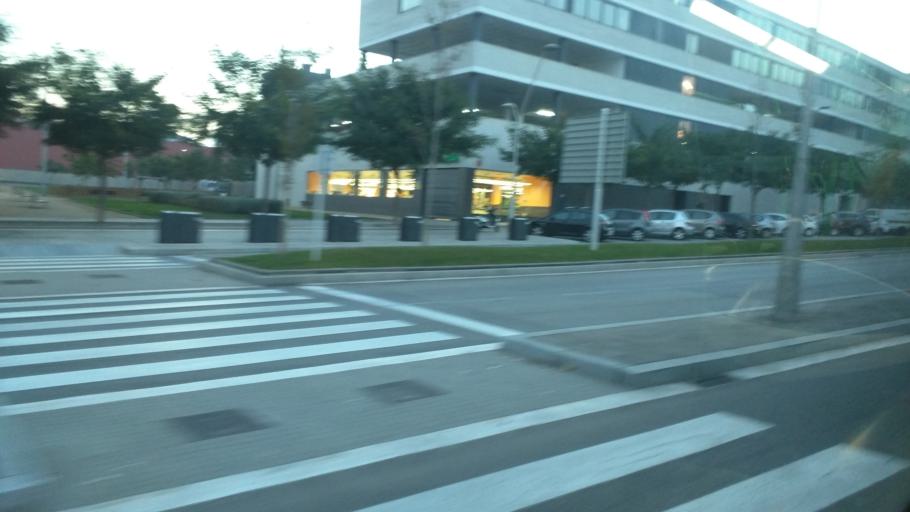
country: ES
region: Catalonia
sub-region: Provincia de Barcelona
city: Sant Feliu de Llobregat
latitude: 41.3766
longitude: 2.0408
